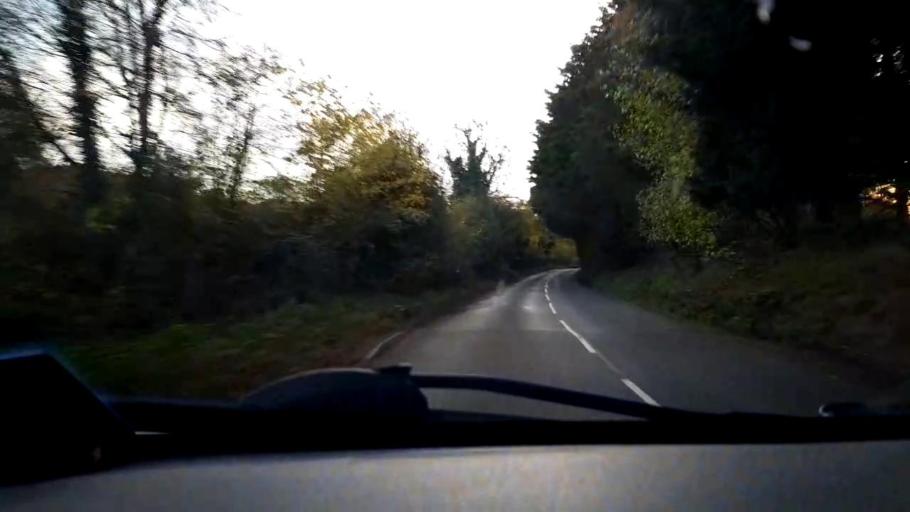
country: GB
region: England
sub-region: Norfolk
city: Mattishall
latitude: 52.7156
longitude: 1.1120
